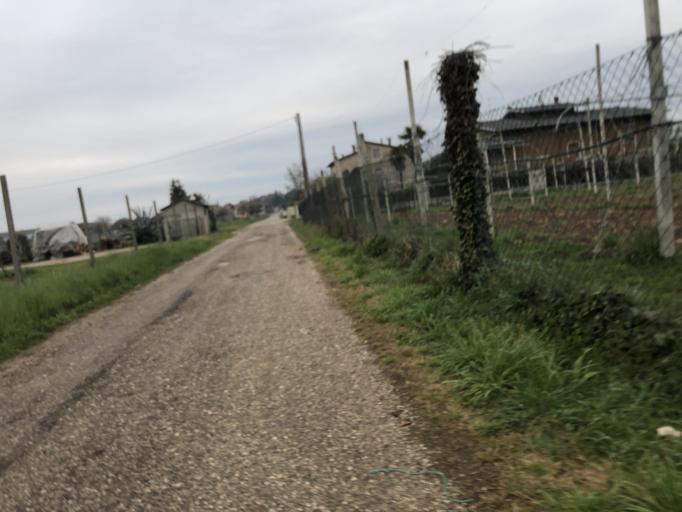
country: IT
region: Veneto
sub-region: Provincia di Verona
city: Sommacampagna
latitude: 45.4043
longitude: 10.8556
